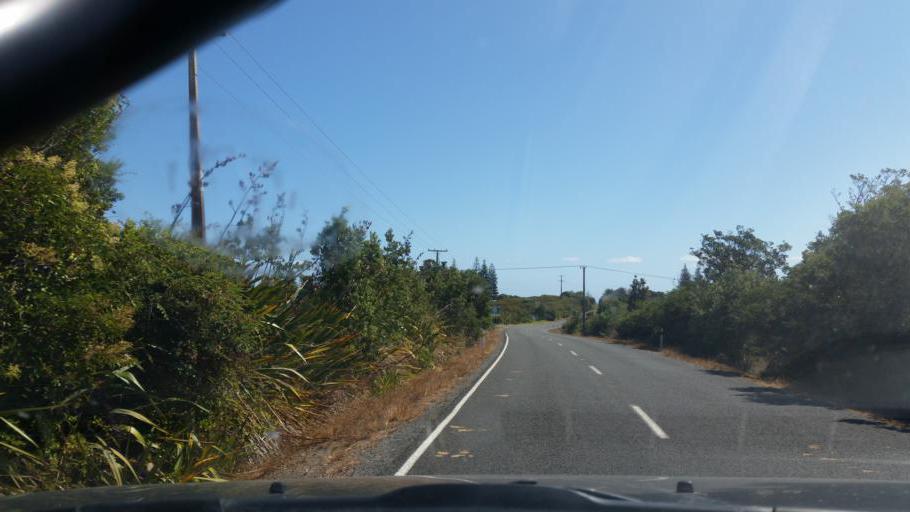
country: NZ
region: Northland
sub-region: Kaipara District
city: Dargaville
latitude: -35.9493
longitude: 173.7591
